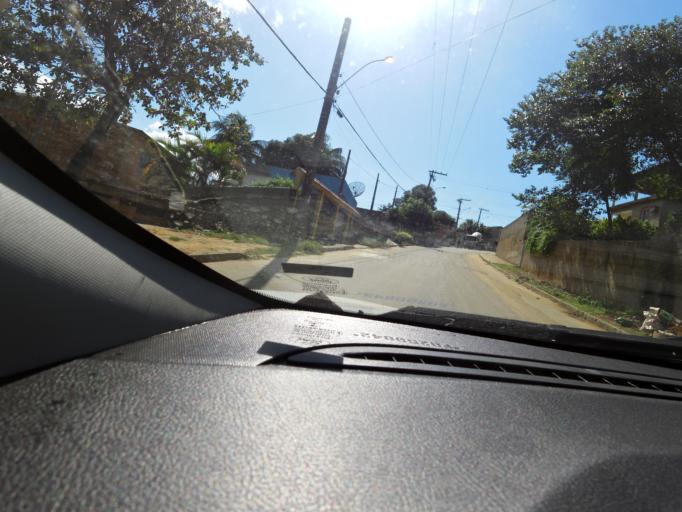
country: BR
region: Espirito Santo
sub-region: Guarapari
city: Guarapari
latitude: -20.6475
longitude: -40.5175
